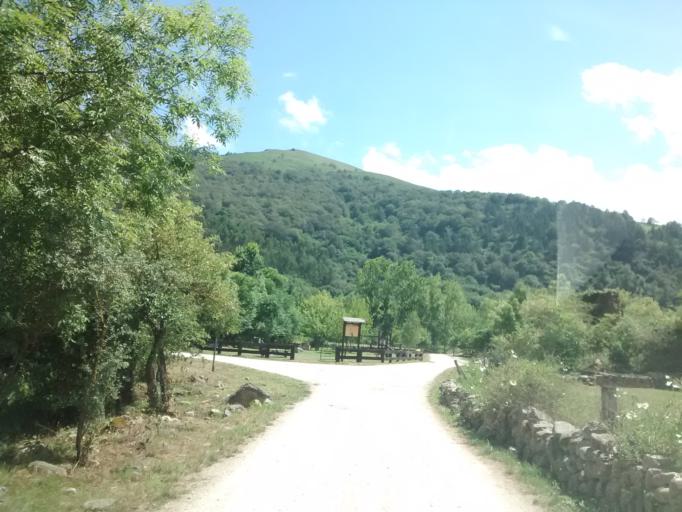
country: ES
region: Cantabria
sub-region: Provincia de Cantabria
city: Ruente
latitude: 43.2176
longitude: -4.2969
